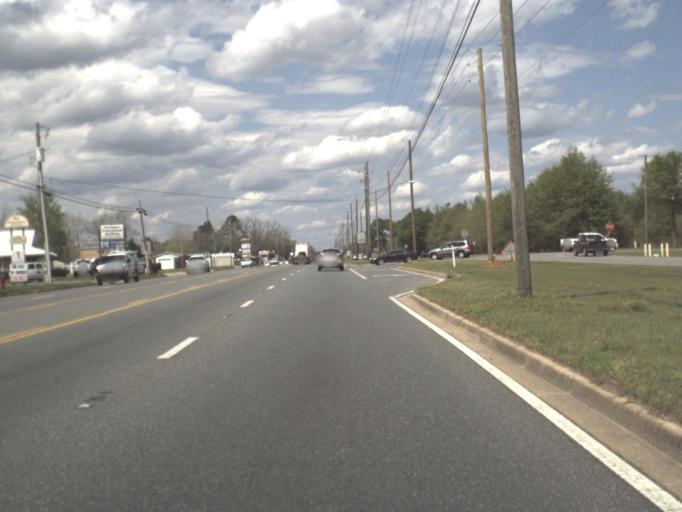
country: US
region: Florida
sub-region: Okaloosa County
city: Crestview
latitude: 30.7794
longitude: -86.5611
